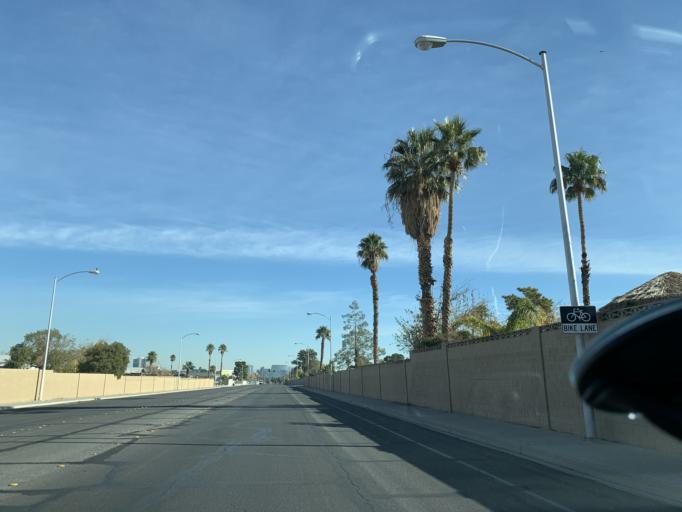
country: US
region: Nevada
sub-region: Clark County
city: Spring Valley
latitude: 36.1071
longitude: -115.2331
